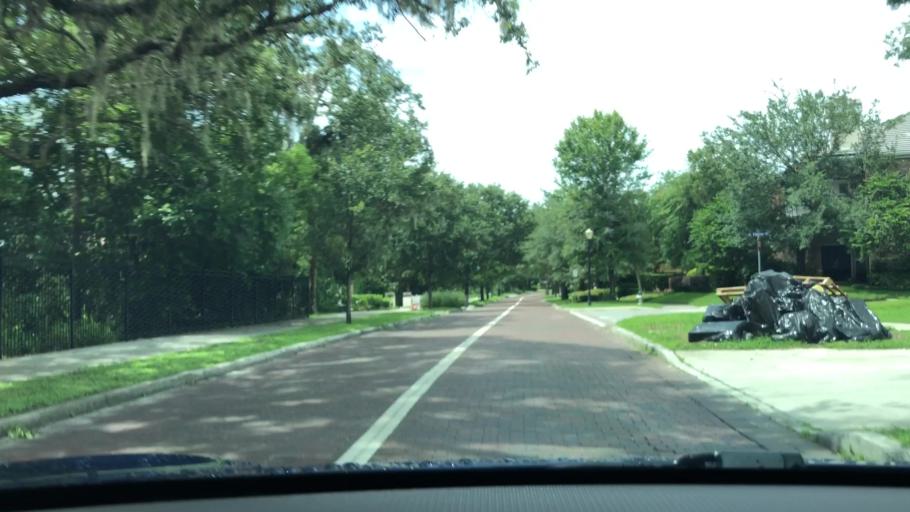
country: US
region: Florida
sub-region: Orange County
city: Winter Park
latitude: 28.5860
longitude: -81.3560
